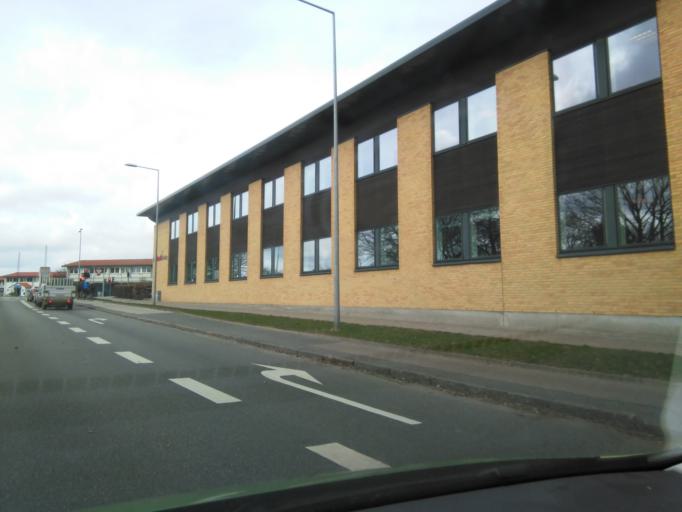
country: DK
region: Central Jutland
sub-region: Arhus Kommune
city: Arhus
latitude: 56.1760
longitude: 10.1799
